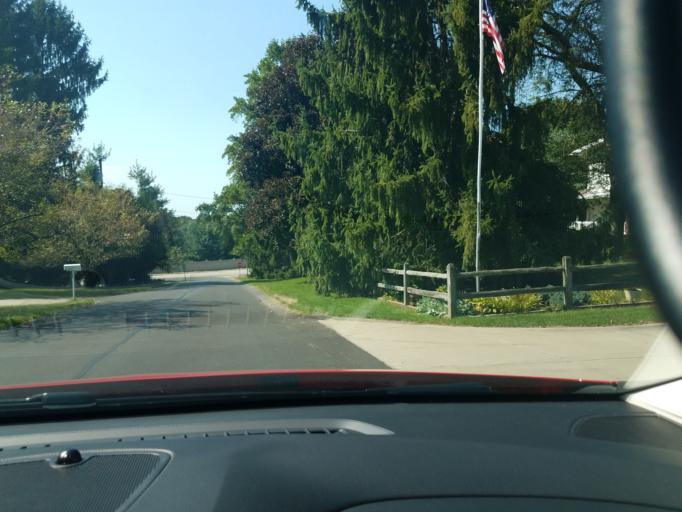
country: US
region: Pennsylvania
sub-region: Allegheny County
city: Franklin Park
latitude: 40.5694
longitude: -80.0763
